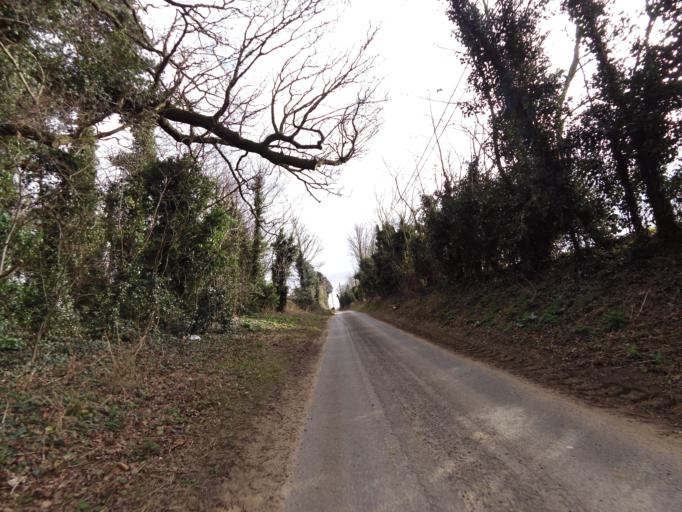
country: GB
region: England
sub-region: Suffolk
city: Woodbridge
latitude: 52.0480
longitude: 1.3270
